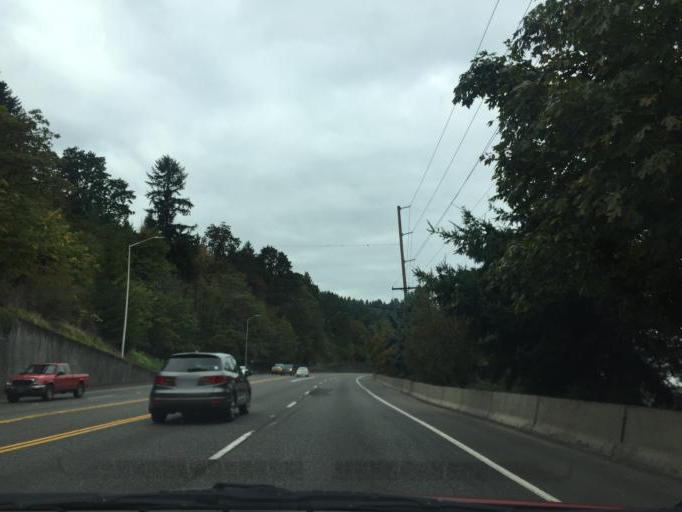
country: US
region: Oregon
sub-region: Washington County
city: West Haven
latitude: 45.5895
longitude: -122.7769
